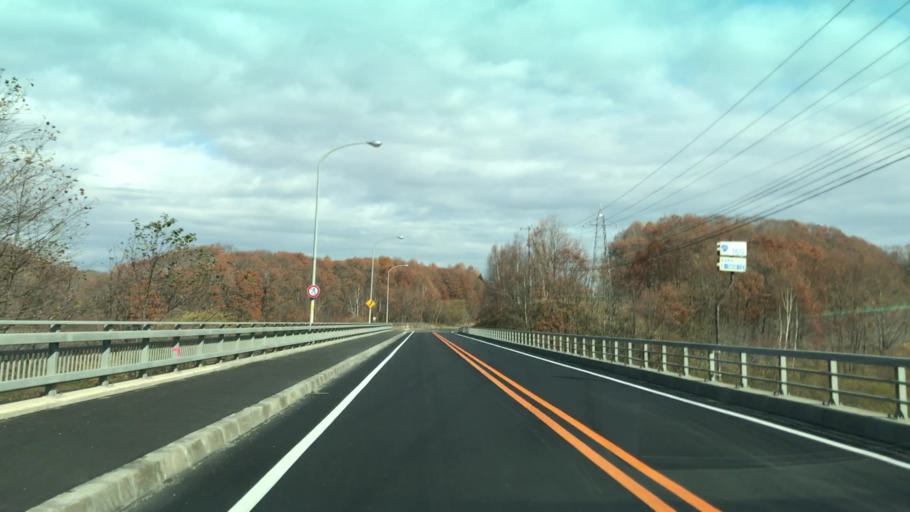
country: JP
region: Hokkaido
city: Shizunai-furukawacho
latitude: 42.6480
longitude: 142.1632
